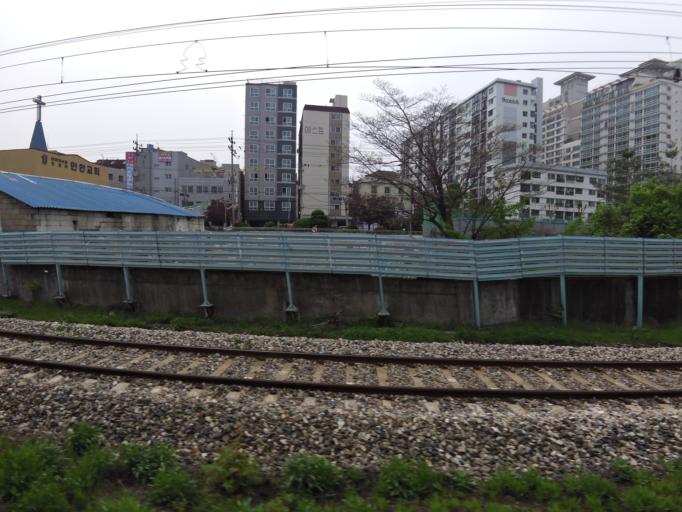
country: KR
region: Gyeonggi-do
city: Anyang-si
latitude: 37.3907
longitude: 126.9332
